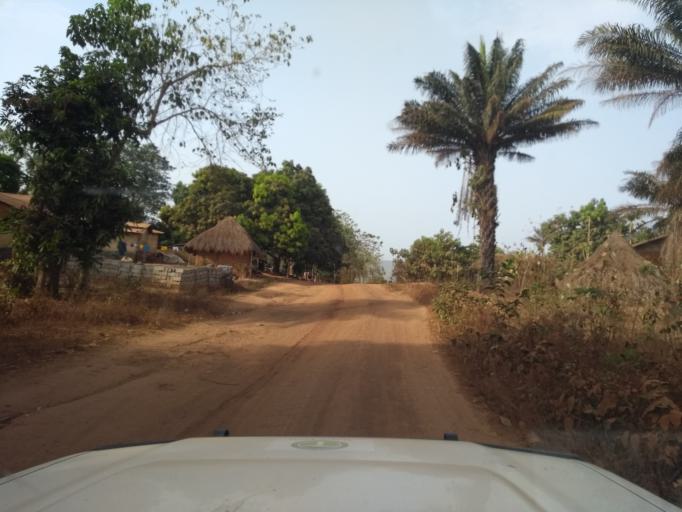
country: GN
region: Kindia
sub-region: Prefecture de Dubreka
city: Dubreka
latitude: 9.8772
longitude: -13.5413
